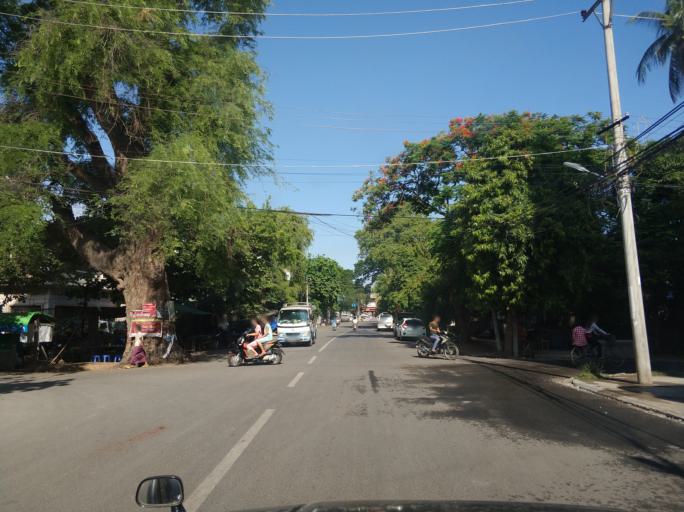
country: MM
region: Mandalay
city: Mandalay
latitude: 21.9729
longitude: 96.0740
